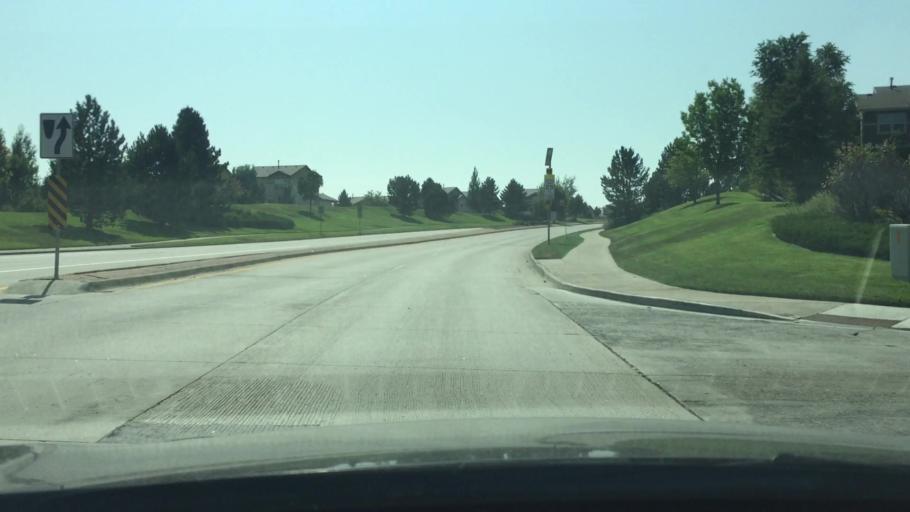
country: US
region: Colorado
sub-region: Arapahoe County
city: Dove Valley
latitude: 39.6050
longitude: -104.7874
